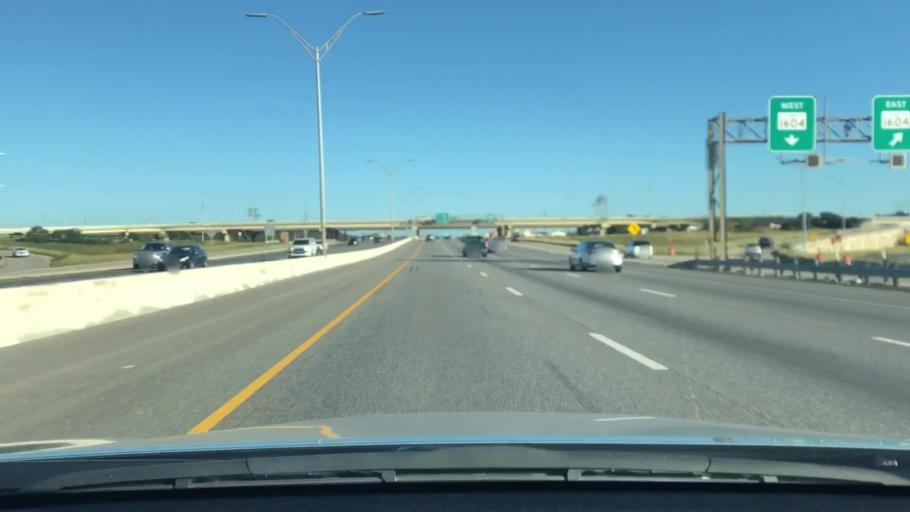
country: US
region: Texas
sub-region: Bexar County
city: Shavano Park
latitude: 29.5885
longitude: -98.5977
